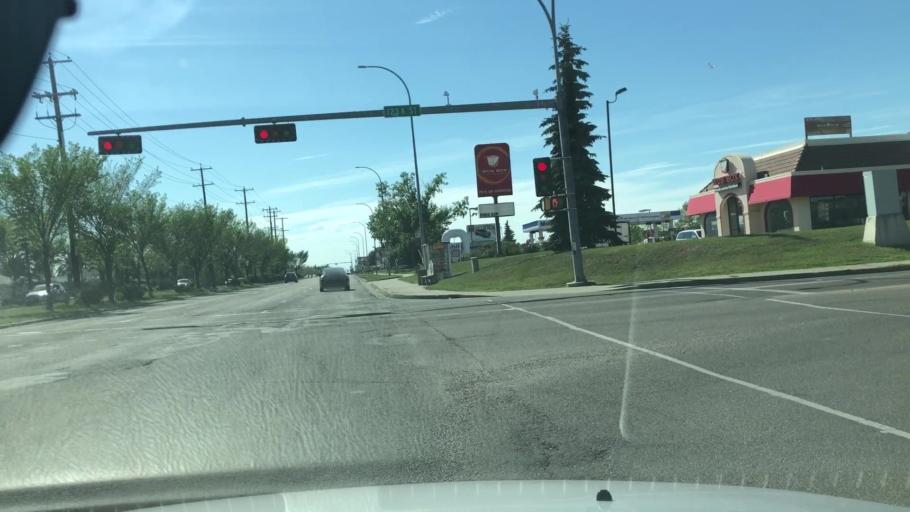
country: CA
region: Alberta
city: Edmonton
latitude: 53.5997
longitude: -113.5347
